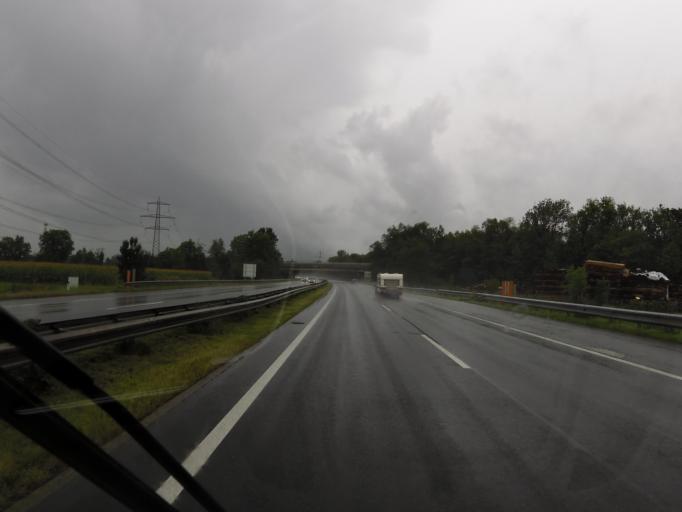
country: AT
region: Vorarlberg
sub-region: Politischer Bezirk Dornbirn
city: Dornbirn
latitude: 47.4264
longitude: 9.7172
